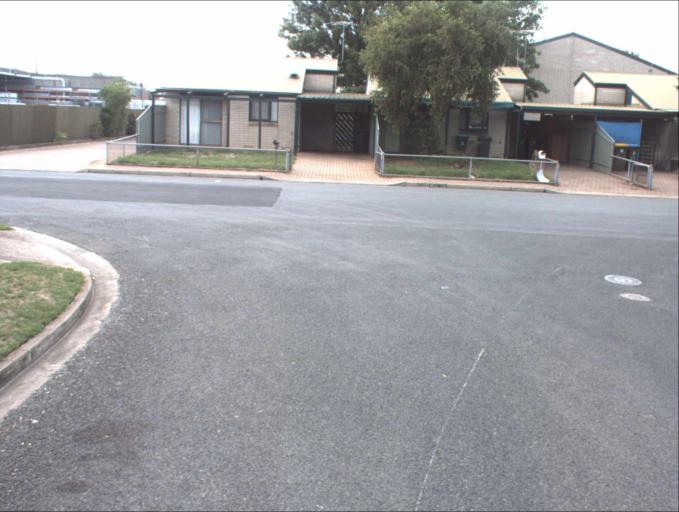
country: AU
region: South Australia
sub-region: Port Adelaide Enfield
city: Enfield
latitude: -34.8496
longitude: 138.5953
